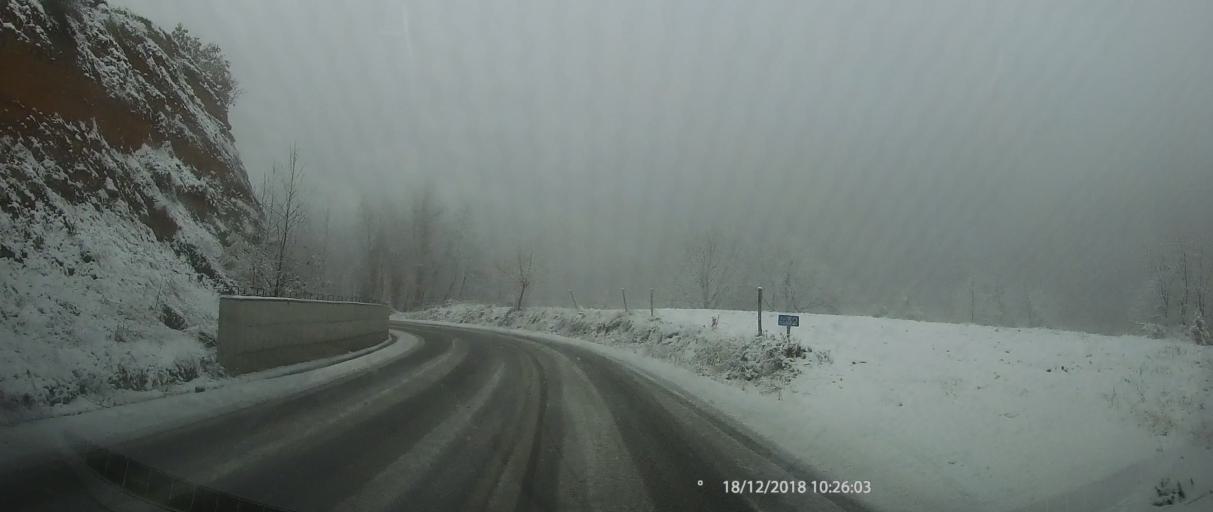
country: GR
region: Thessaly
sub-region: Nomos Larisis
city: Livadi
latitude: 40.1680
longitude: 22.2501
